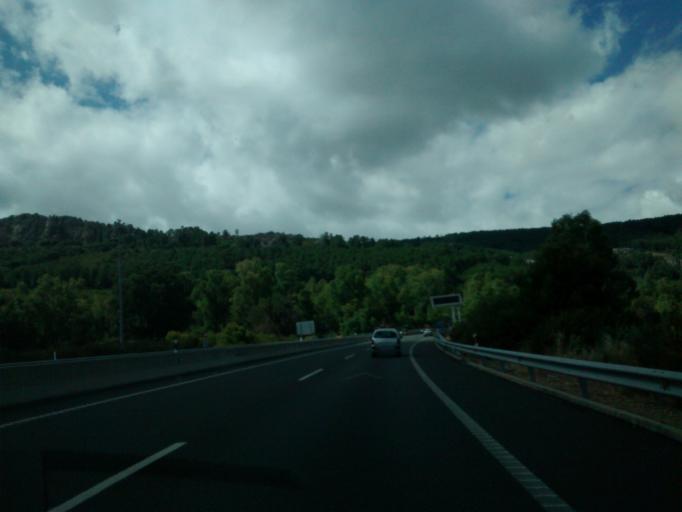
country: ES
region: Extremadura
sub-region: Provincia de Caceres
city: Higuera
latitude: 39.7016
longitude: -5.6902
